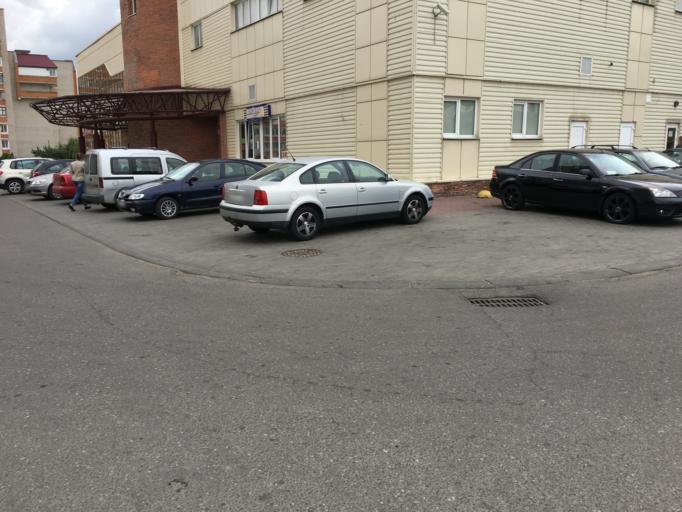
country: BY
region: Grodnenskaya
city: Hrodna
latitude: 53.7120
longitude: 23.8483
